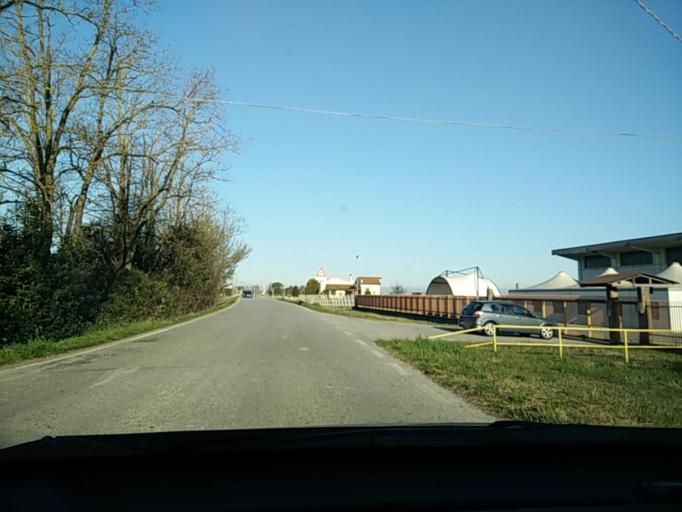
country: IT
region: Veneto
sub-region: Provincia di Venezia
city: Iesolo
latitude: 45.5513
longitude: 12.6621
